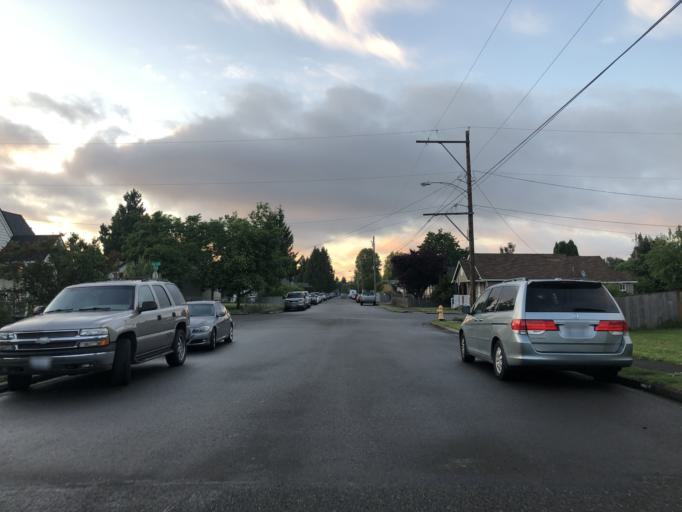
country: US
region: Washington
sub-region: King County
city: Auburn
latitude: 47.3095
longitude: -122.2096
